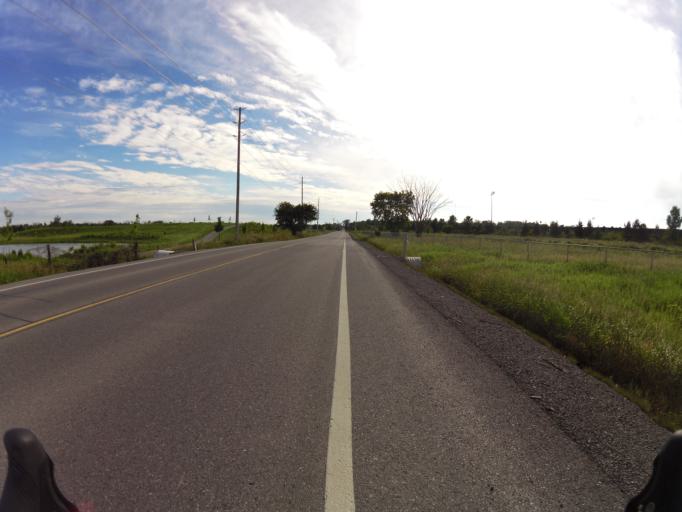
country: CA
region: Ontario
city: Bells Corners
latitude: 45.2587
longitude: -75.7754
